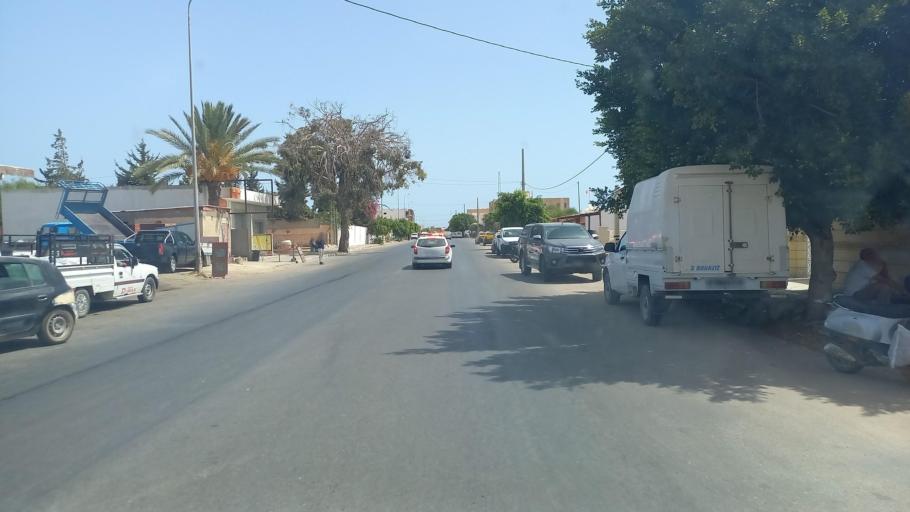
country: TN
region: Madanin
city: Zarzis
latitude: 33.4952
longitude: 11.0840
